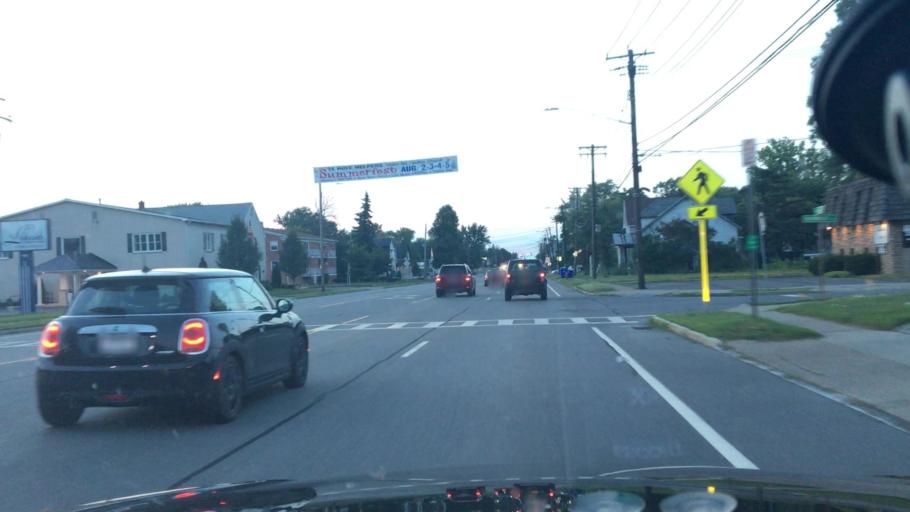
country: US
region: New York
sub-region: Erie County
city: West Seneca
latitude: 42.8359
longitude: -78.7538
